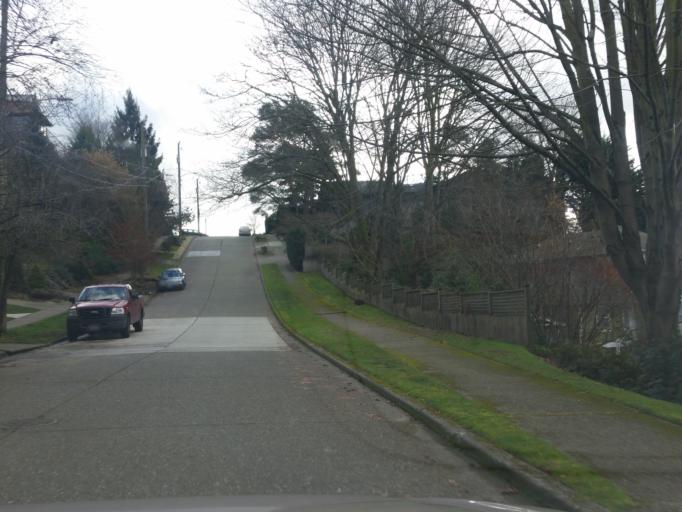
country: US
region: Washington
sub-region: King County
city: Seattle
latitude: 47.6594
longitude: -122.3573
